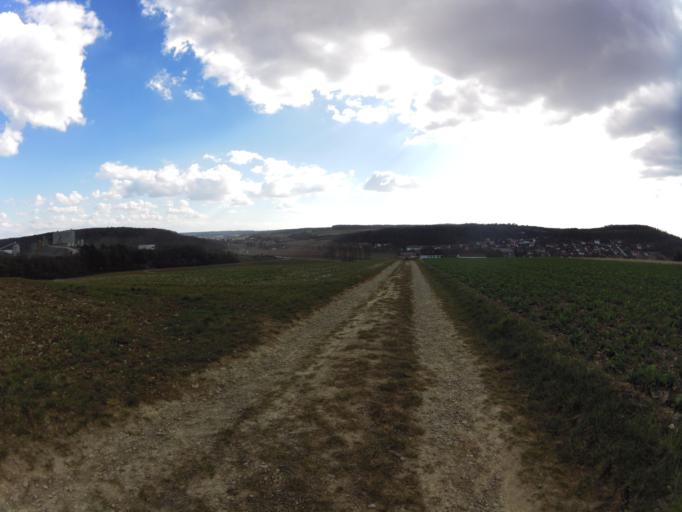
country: DE
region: Bavaria
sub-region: Regierungsbezirk Unterfranken
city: Greussenheim
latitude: 49.8009
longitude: 9.7641
